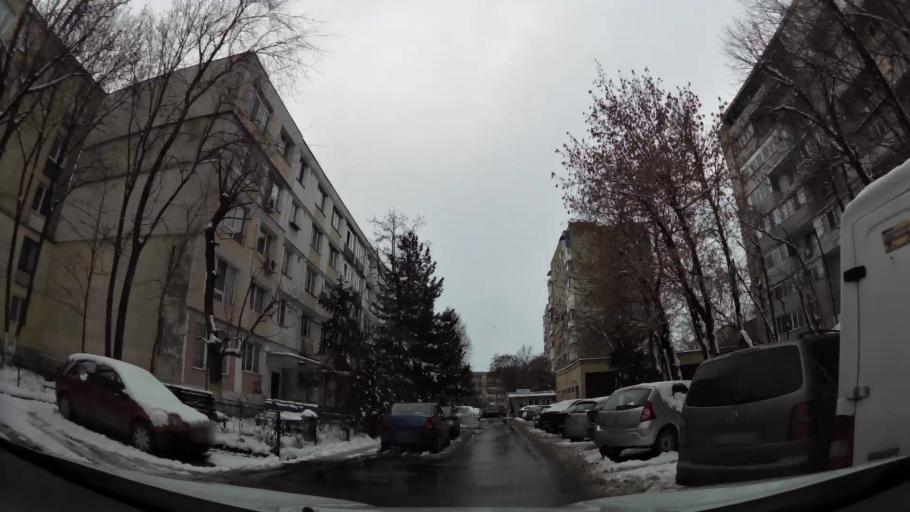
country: RO
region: Bucuresti
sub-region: Municipiul Bucuresti
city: Bucuresti
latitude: 44.3913
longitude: 26.1164
